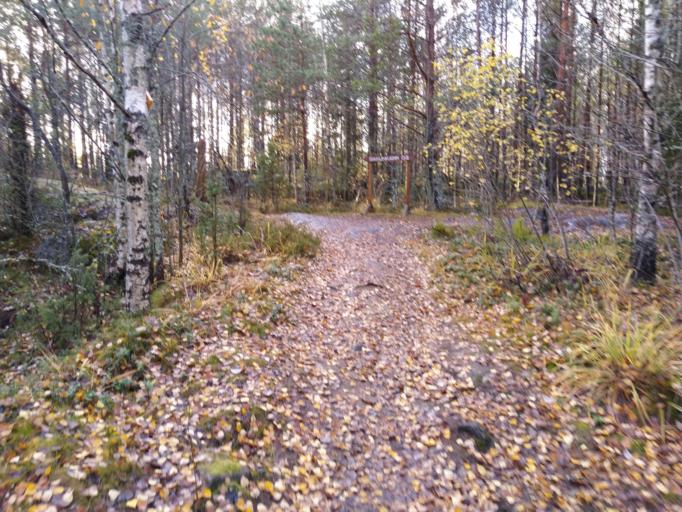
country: FI
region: Uusimaa
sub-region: Helsinki
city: Sibbo
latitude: 60.3058
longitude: 25.2095
